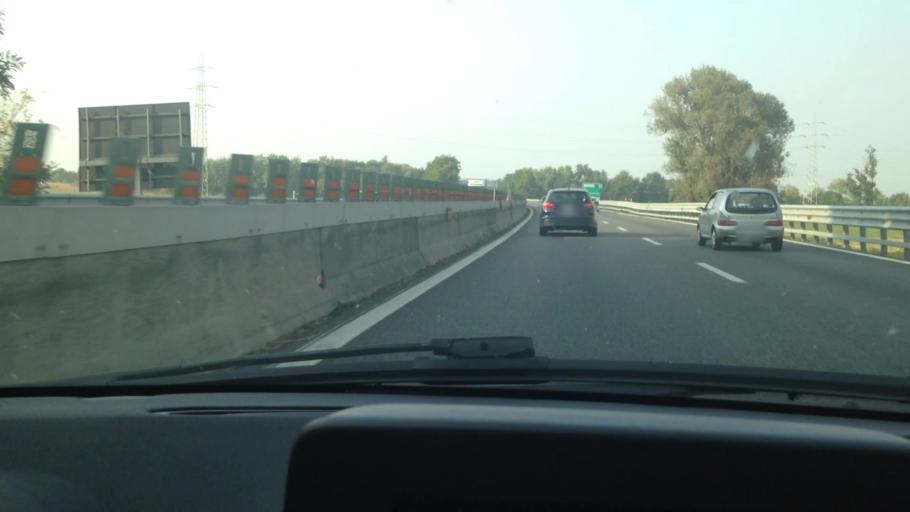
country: IT
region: Piedmont
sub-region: Provincia di Torino
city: Borgaro Torinese
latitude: 45.1622
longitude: 7.6857
